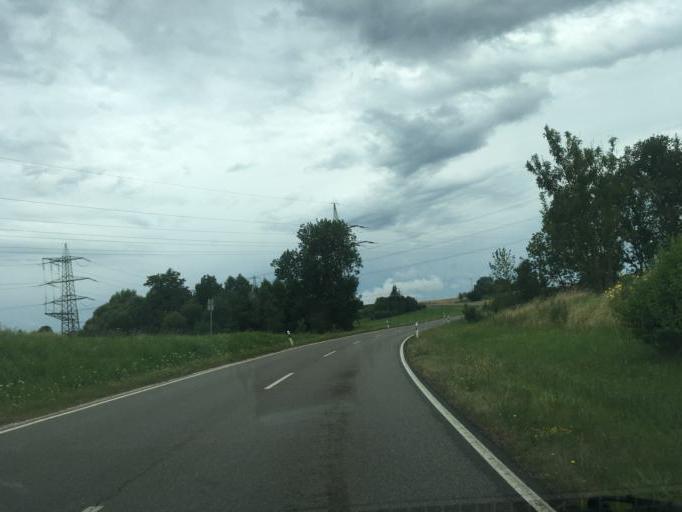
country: DE
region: Baden-Wuerttemberg
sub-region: Tuebingen Region
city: Pliezhausen
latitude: 48.5318
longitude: 9.2222
